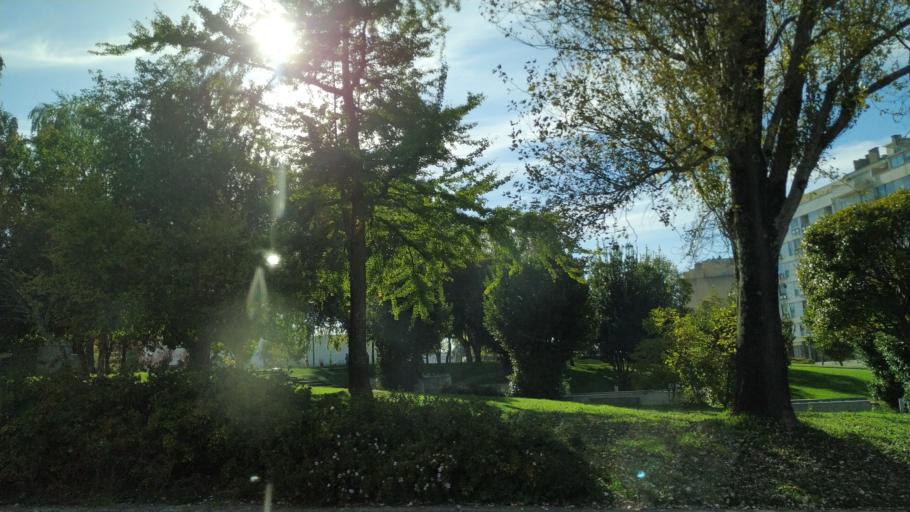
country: PT
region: Porto
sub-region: Vila Nova de Gaia
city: Vila Nova de Gaia
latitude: 41.1231
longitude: -8.6117
